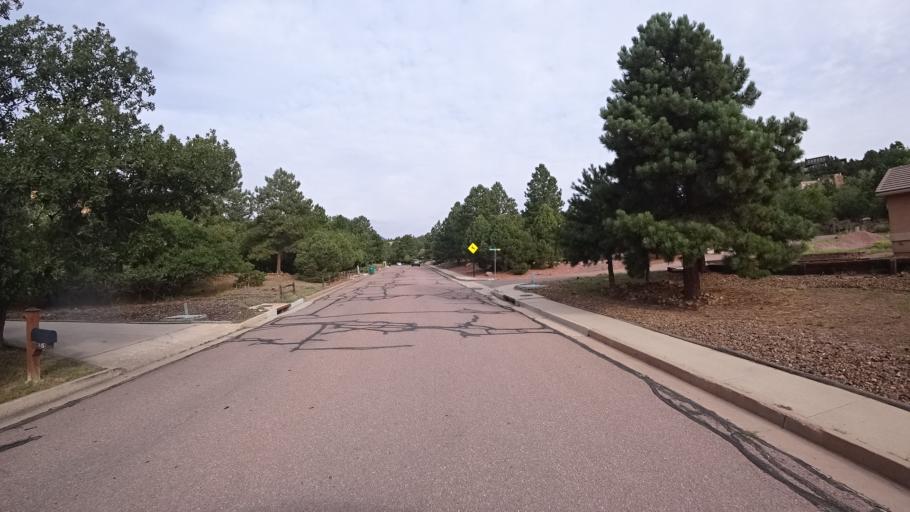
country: US
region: Colorado
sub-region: El Paso County
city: Air Force Academy
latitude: 38.9331
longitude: -104.8483
